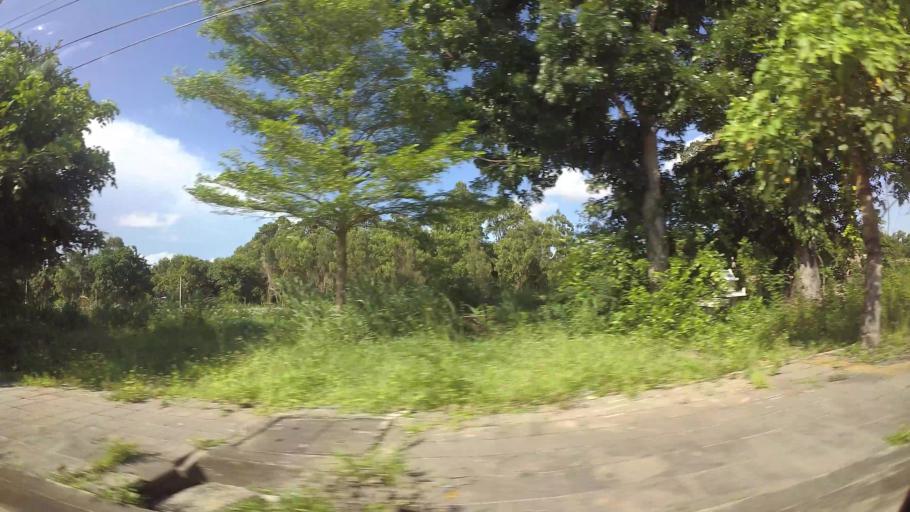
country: TH
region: Rayong
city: Rayong
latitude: 12.6772
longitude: 101.2943
